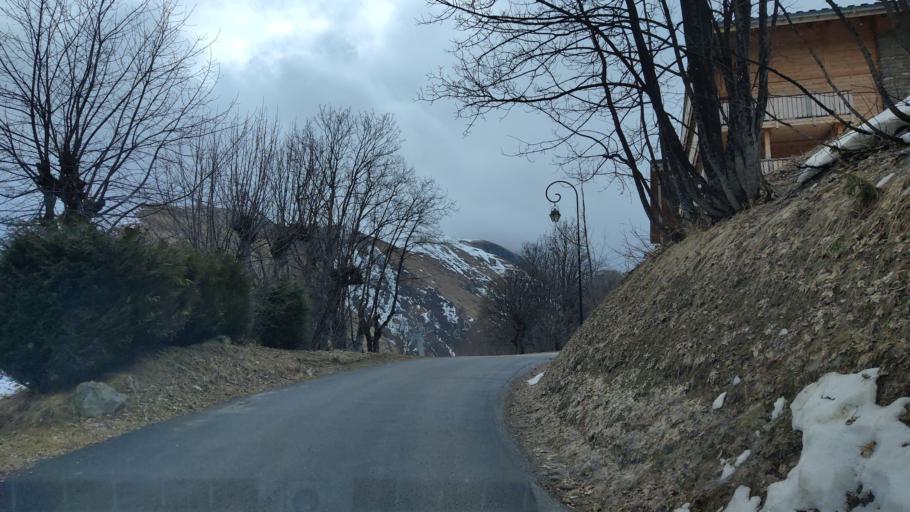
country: FR
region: Rhone-Alpes
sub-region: Departement de la Savoie
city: Saint-Jean-de-Maurienne
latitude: 45.2184
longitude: 6.2247
